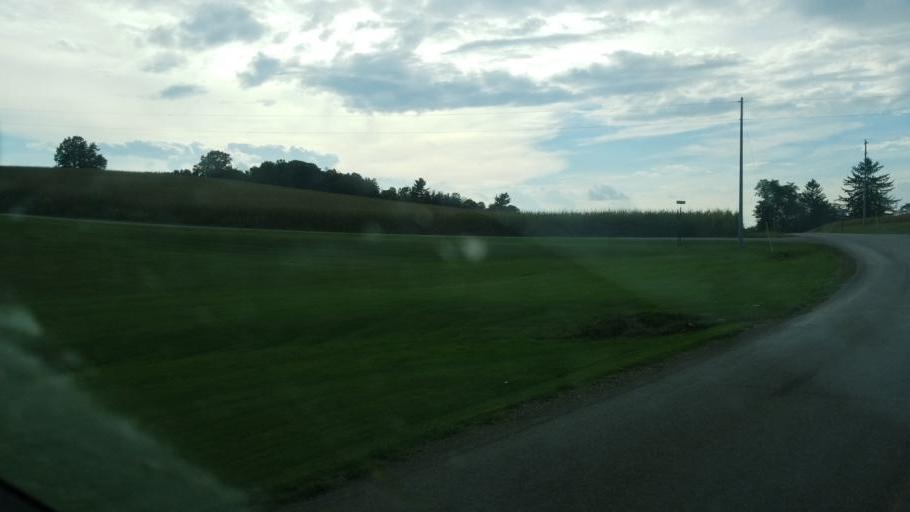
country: US
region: Ohio
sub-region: Knox County
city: Danville
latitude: 40.4696
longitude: -82.3256
